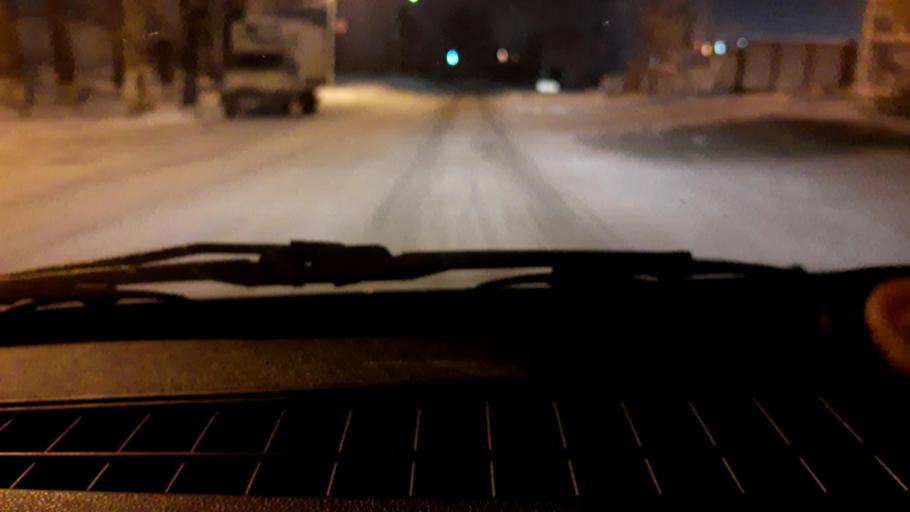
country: RU
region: Bashkortostan
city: Ufa
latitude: 54.8262
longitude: 56.0761
